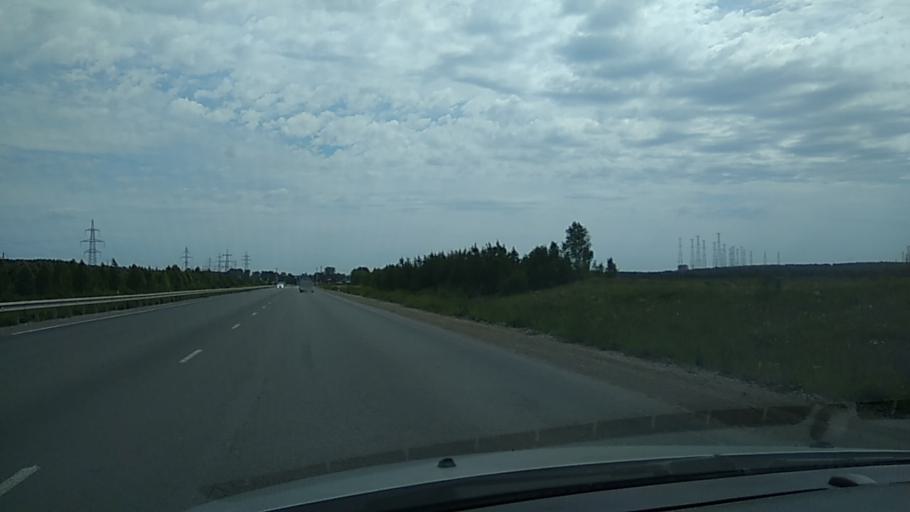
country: RU
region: Sverdlovsk
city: Verkhnyaya Pyshma
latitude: 56.9515
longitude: 60.5882
